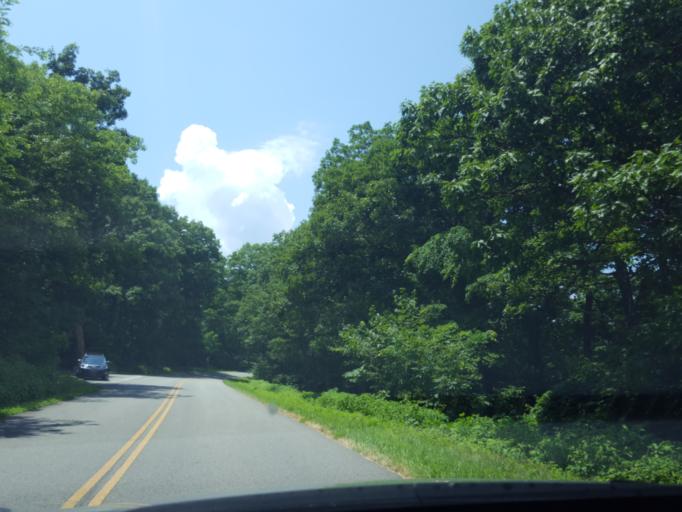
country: US
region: Virginia
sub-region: Nelson County
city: Nellysford
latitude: 37.9414
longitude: -78.9355
